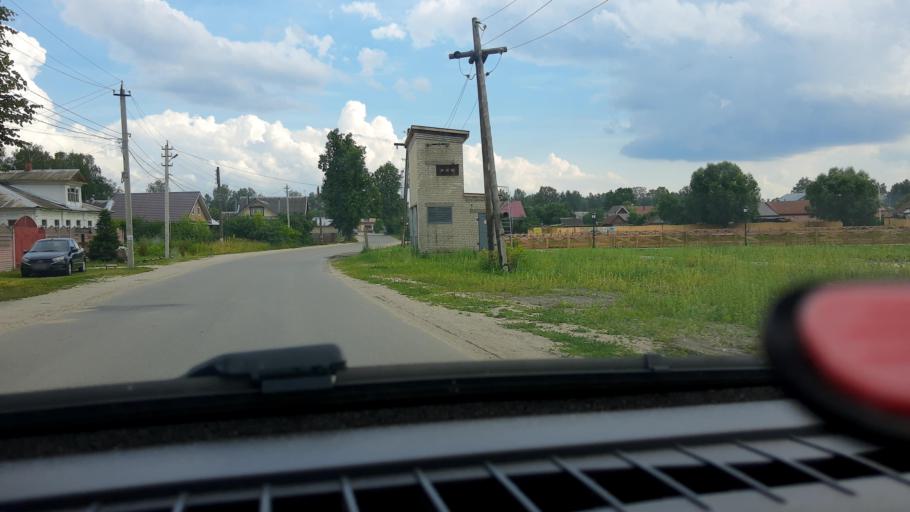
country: RU
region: Nizjnij Novgorod
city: Gorodets
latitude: 56.6372
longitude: 43.4746
